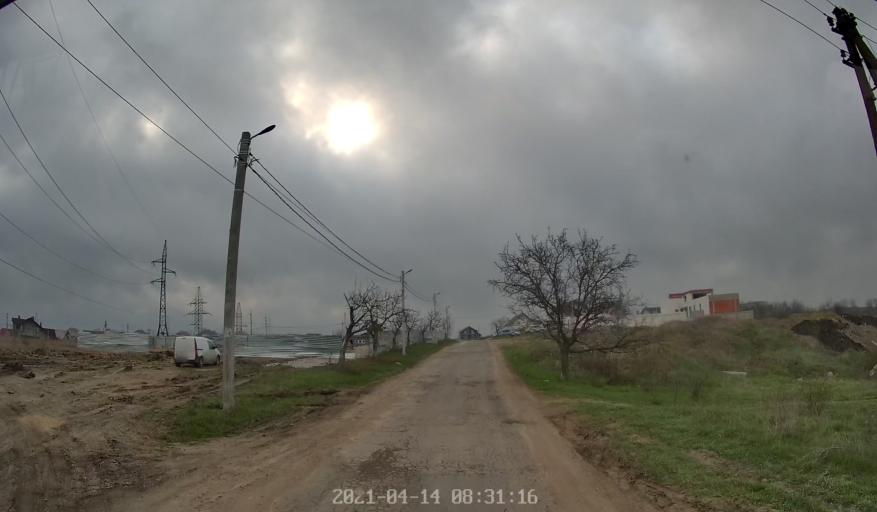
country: MD
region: Chisinau
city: Stauceni
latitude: 47.0617
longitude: 28.9336
